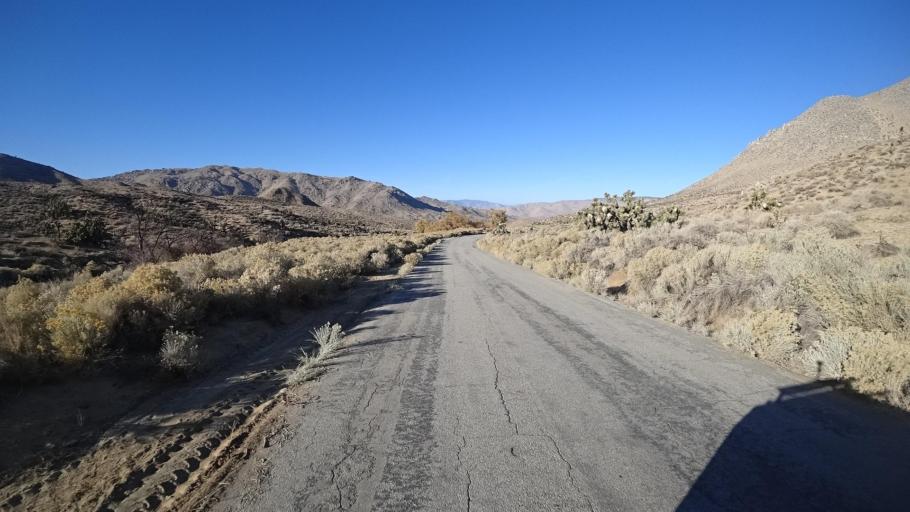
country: US
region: California
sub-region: Kern County
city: Weldon
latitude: 35.4651
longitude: -118.2113
